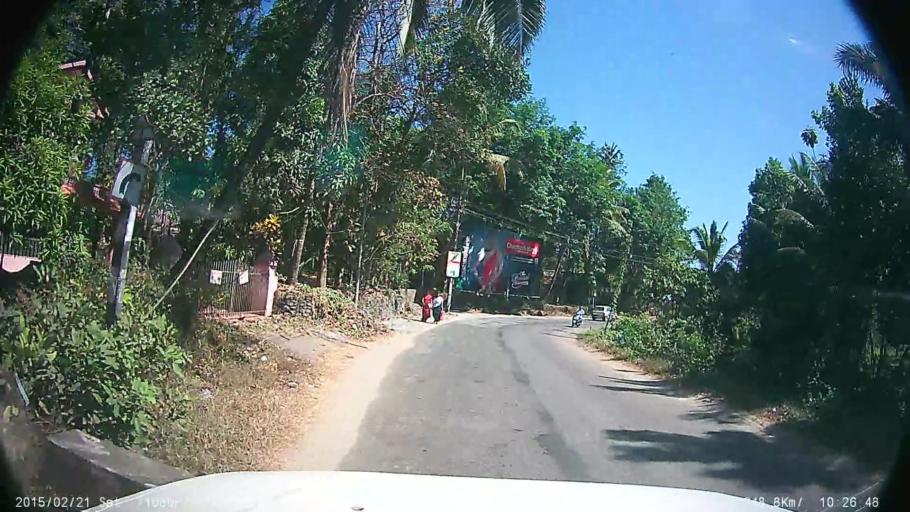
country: IN
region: Kerala
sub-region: Kottayam
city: Palackattumala
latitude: 9.8551
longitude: 76.6878
